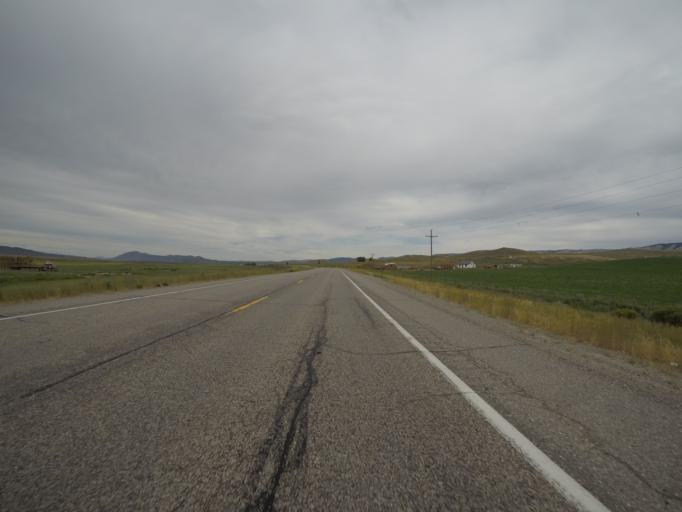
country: US
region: Utah
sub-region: Rich County
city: Randolph
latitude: 41.9934
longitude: -110.9401
